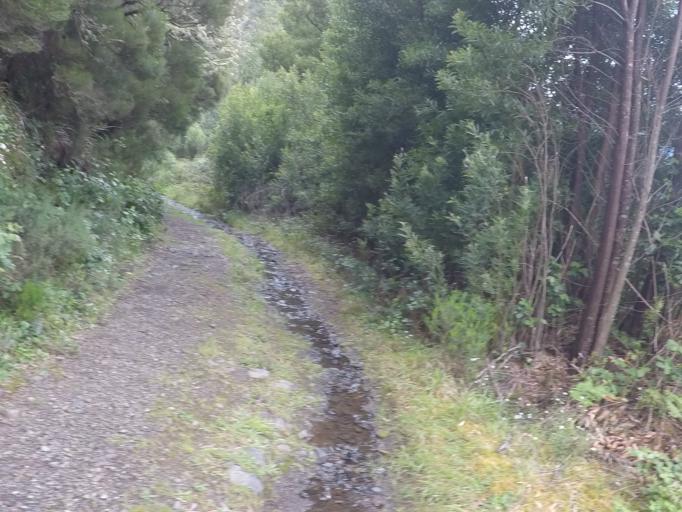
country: PT
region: Madeira
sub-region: Sao Vicente
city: Sao Vicente
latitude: 32.7519
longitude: -17.0187
